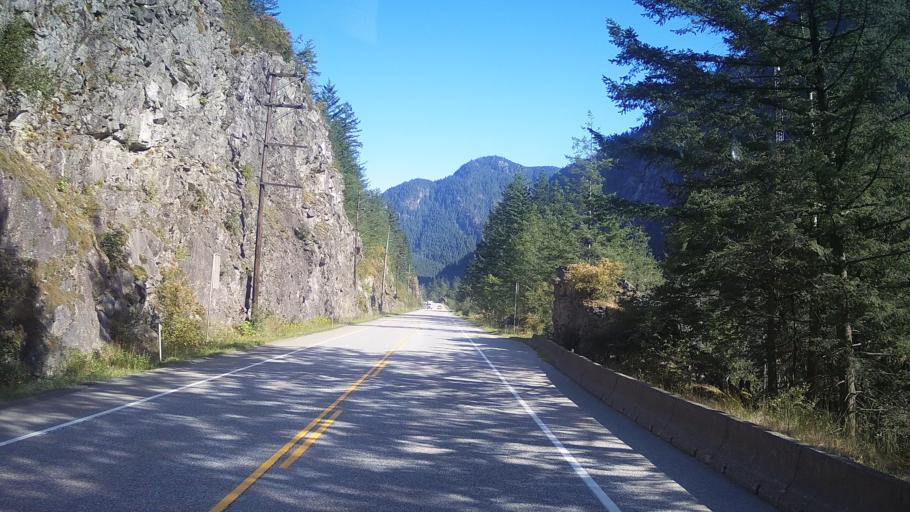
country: CA
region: British Columbia
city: Hope
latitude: 49.5812
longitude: -121.4027
